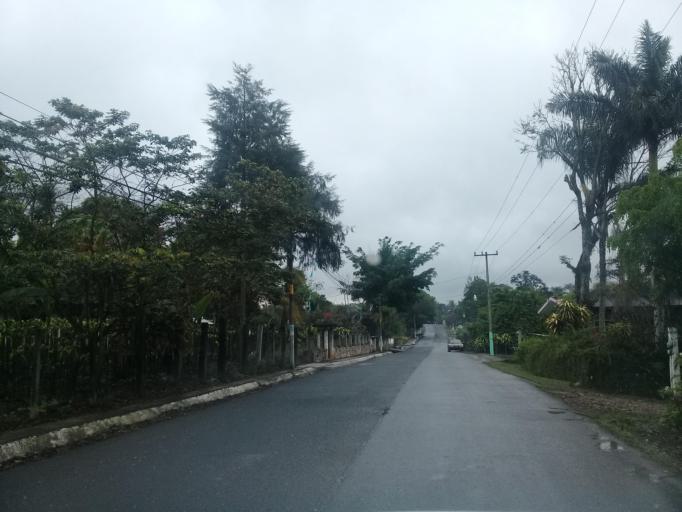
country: MX
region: Veracruz
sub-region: Amatlan de los Reyes
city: Trapiche Viejo
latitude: 18.8262
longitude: -96.9567
